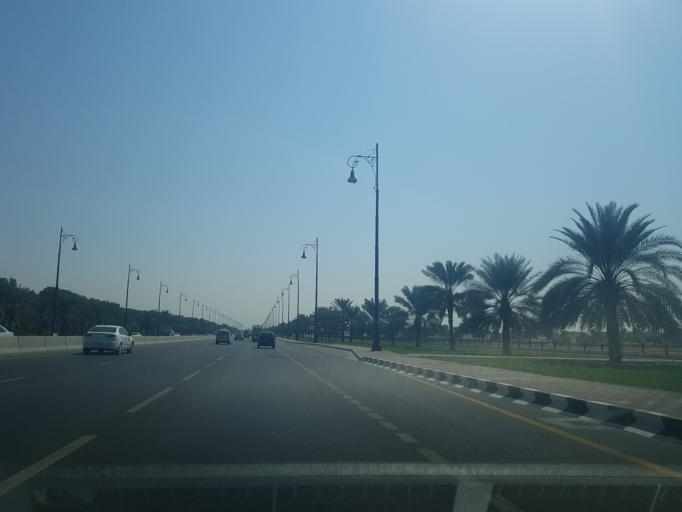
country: AE
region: Ash Shariqah
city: Sharjah
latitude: 25.3213
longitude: 55.5022
